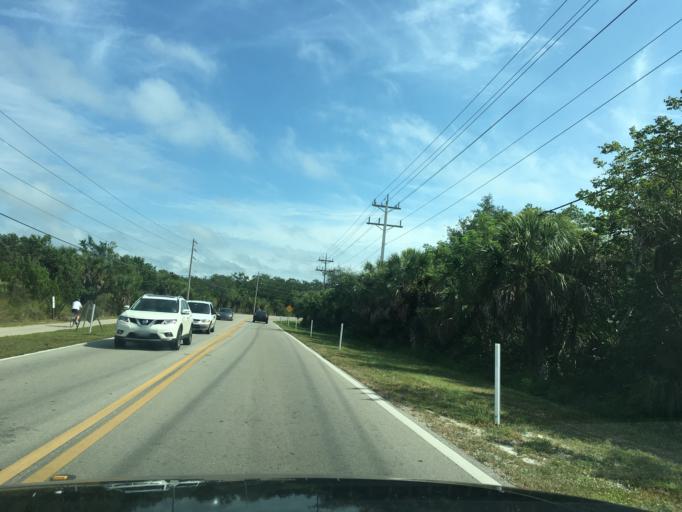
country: US
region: Florida
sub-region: Lee County
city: Saint James City
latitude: 26.4507
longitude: -82.1286
